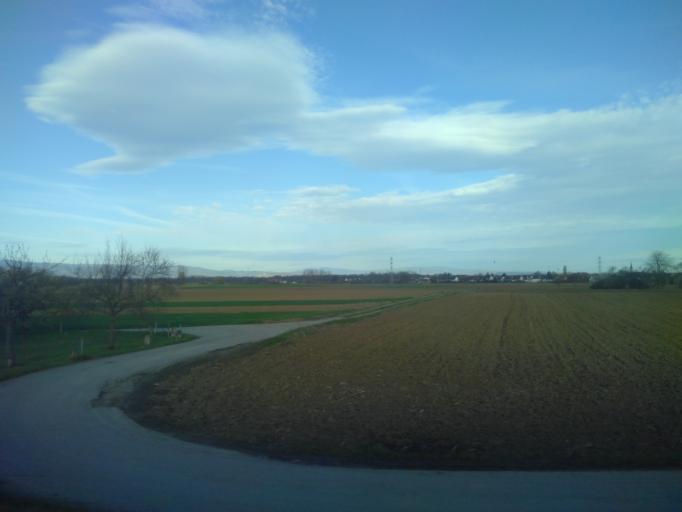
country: FR
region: Alsace
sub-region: Departement du Bas-Rhin
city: Nordhouse
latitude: 48.4491
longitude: 7.6542
